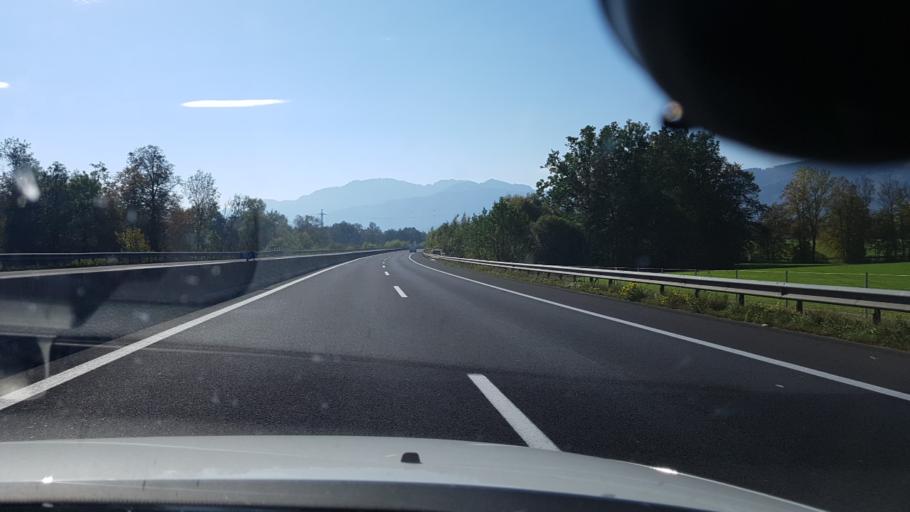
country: AT
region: Upper Austria
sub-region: Politischer Bezirk Kirchdorf an der Krems
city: Micheldorf in Oberoesterreich
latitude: 47.9520
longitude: 14.1016
